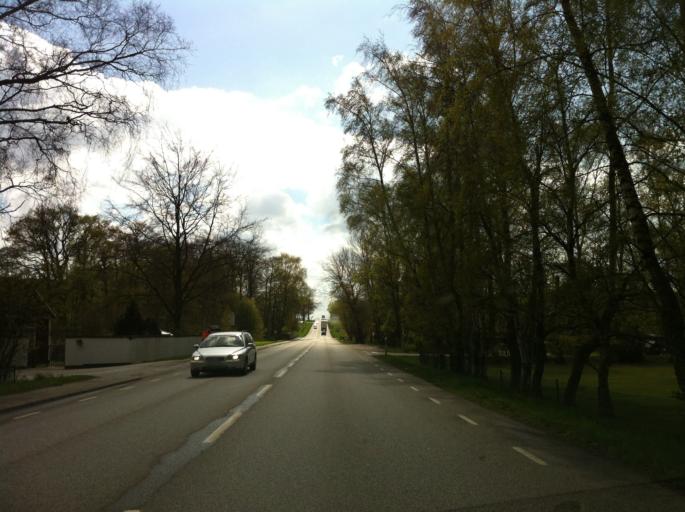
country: SE
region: Skane
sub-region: Hoors Kommun
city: Satofta
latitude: 55.8707
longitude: 13.4946
